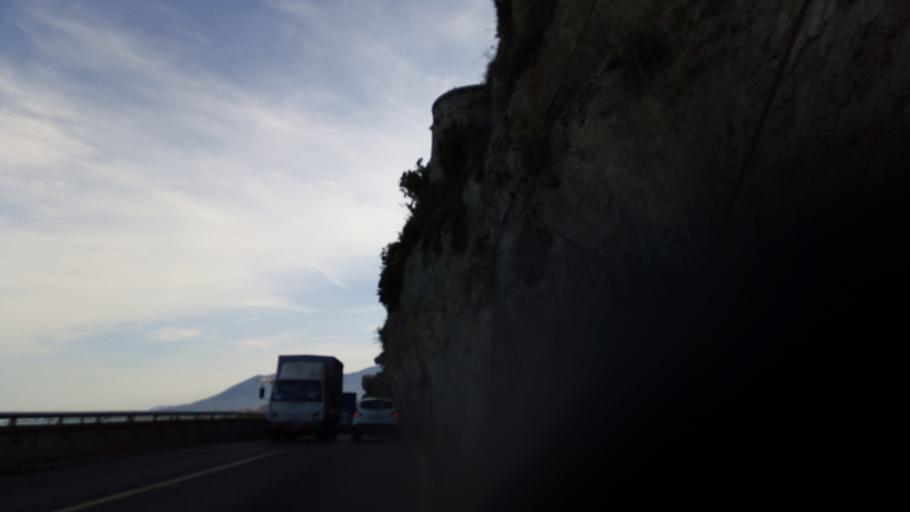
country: IT
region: Liguria
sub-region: Provincia di Savona
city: Borghetto Santo Spirito
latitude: 44.1038
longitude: 8.2385
